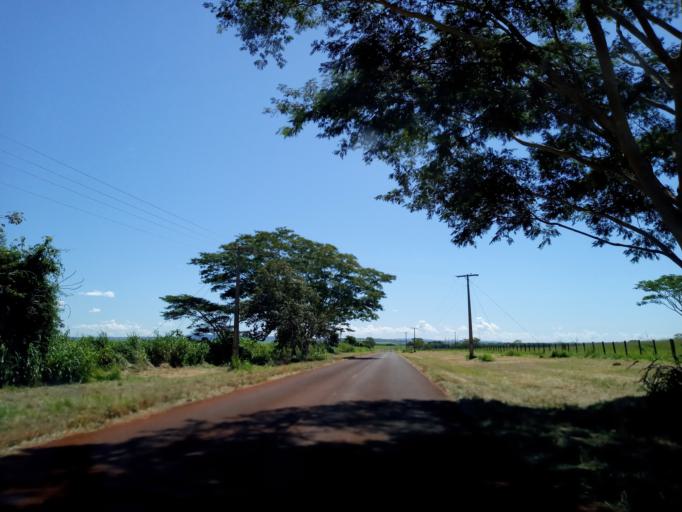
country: BR
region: Goias
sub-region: Itumbiara
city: Itumbiara
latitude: -18.4128
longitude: -49.1299
